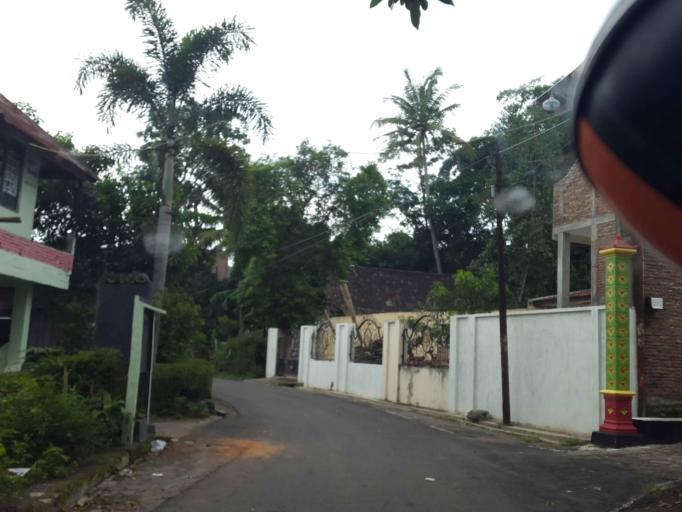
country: ID
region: Central Java
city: Salatiga
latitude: -7.3236
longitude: 110.5128
